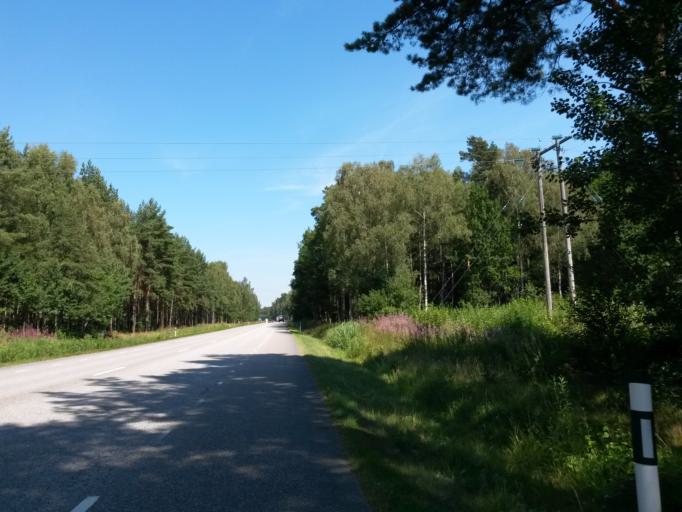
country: SE
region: Vaestra Goetaland
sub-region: Lidkopings Kommun
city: Lidkoping
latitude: 58.4858
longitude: 13.1274
